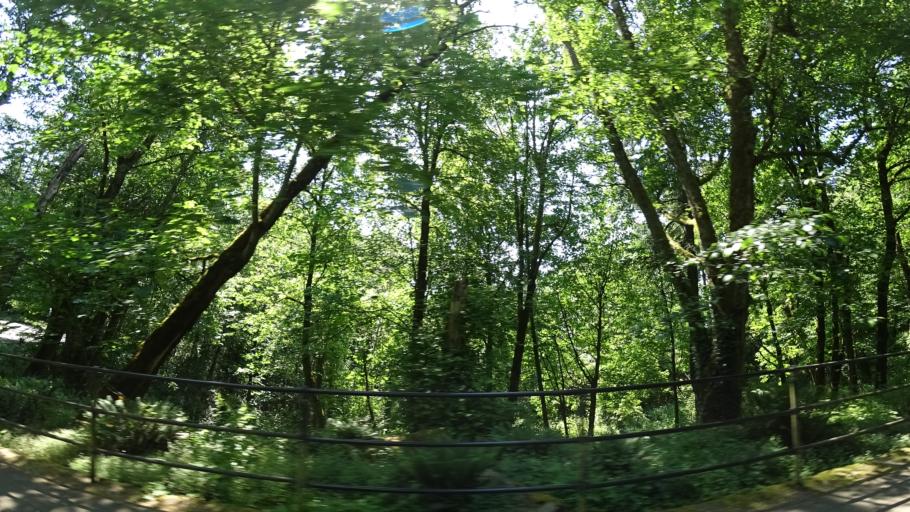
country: US
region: Oregon
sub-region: Clackamas County
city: Lake Oswego
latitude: 45.4283
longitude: -122.7079
